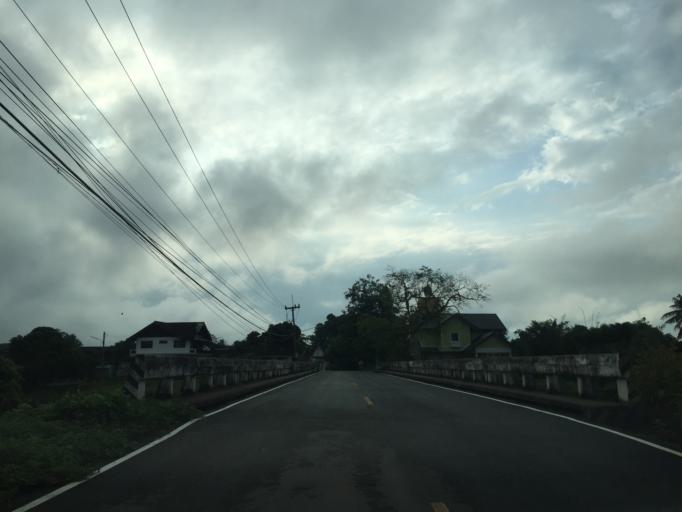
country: TH
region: Lamphun
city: Ban Thi
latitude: 18.6534
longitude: 99.0640
